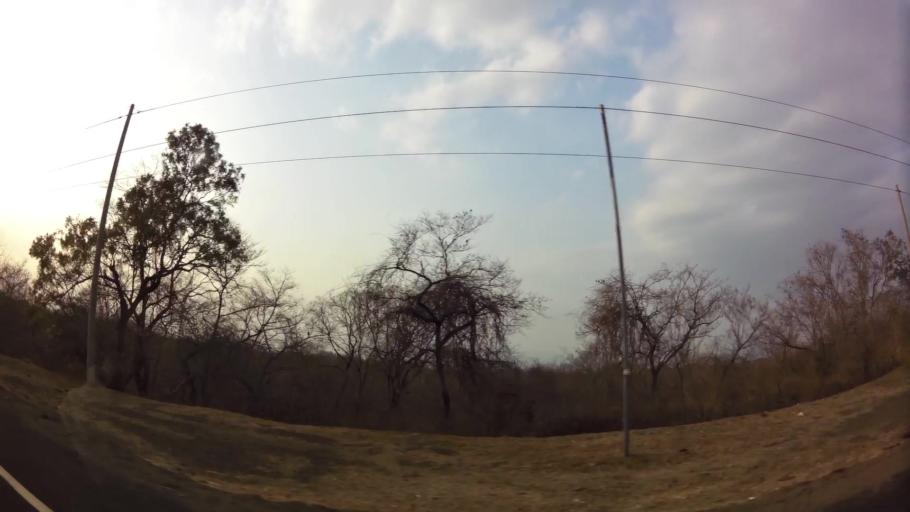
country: NI
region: Leon
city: Nagarote
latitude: 12.2817
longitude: -86.5188
